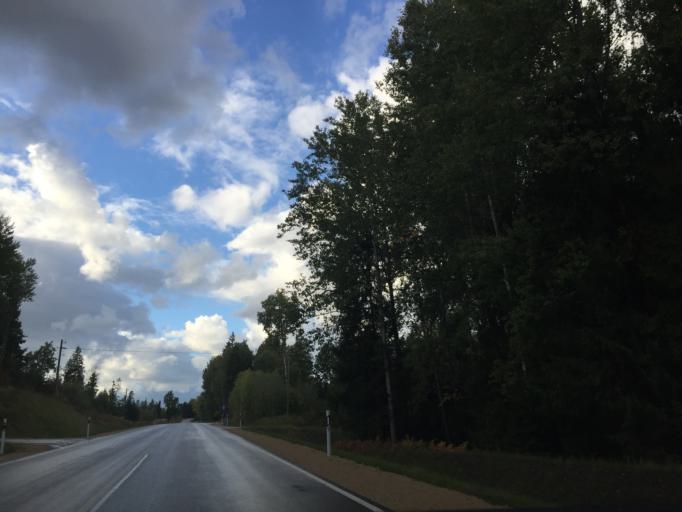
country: LV
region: Ligatne
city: Ligatne
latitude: 57.1600
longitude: 25.0586
